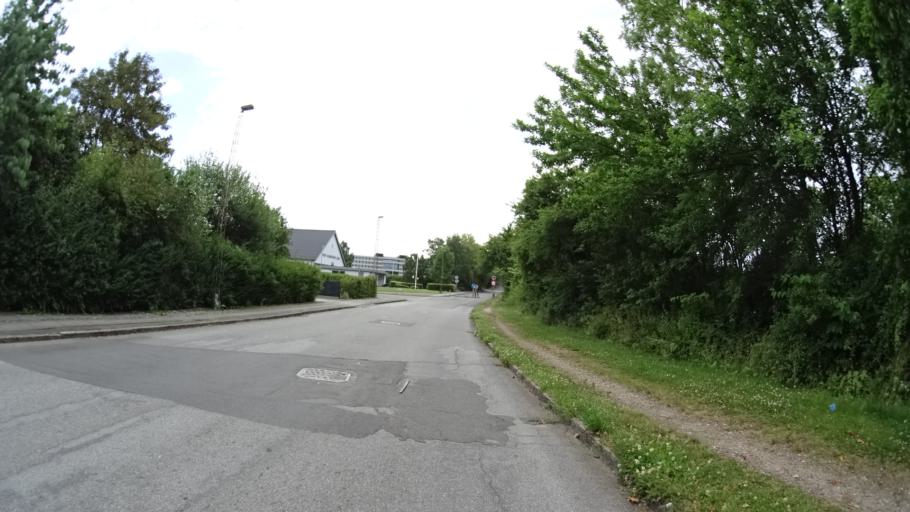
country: DK
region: Central Jutland
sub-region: Arhus Kommune
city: Stavtrup
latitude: 56.1272
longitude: 10.1484
